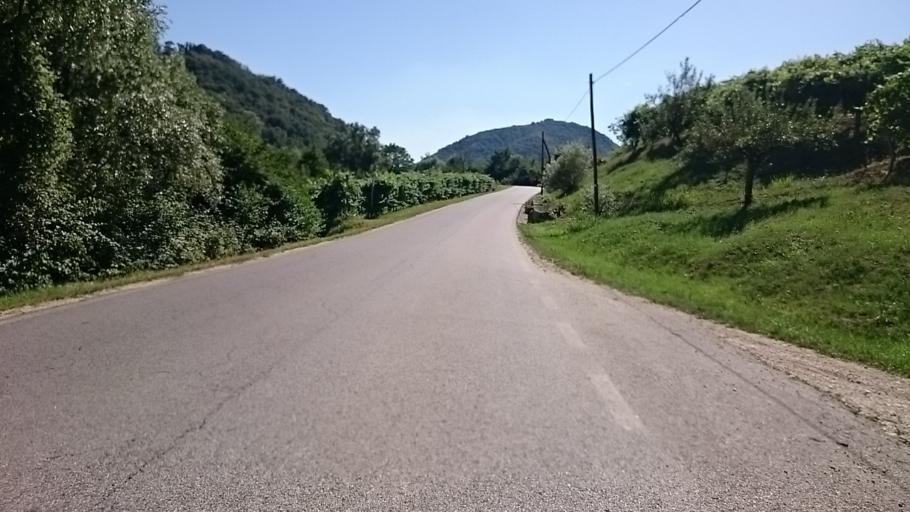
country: IT
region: Veneto
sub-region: Provincia di Treviso
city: Miane
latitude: 45.9164
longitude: 12.0793
